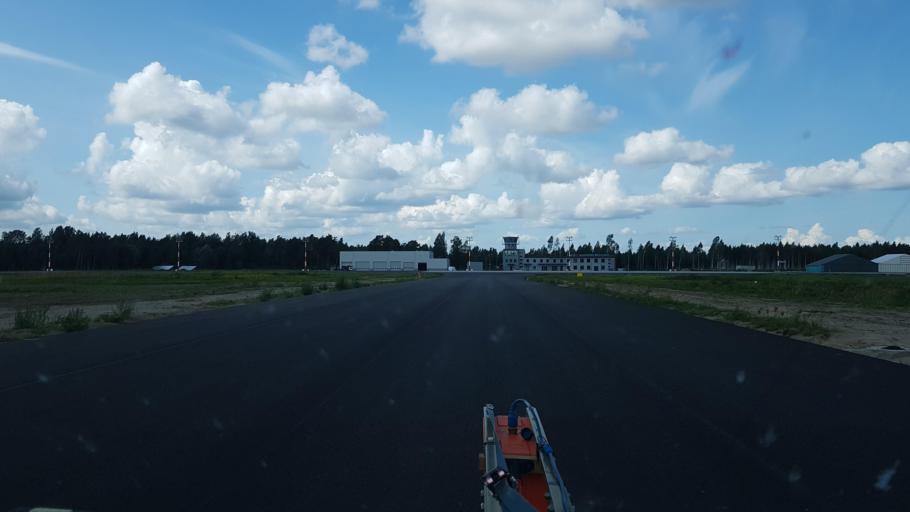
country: EE
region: Paernumaa
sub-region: Sauga vald
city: Sauga
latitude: 58.4192
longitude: 24.4712
